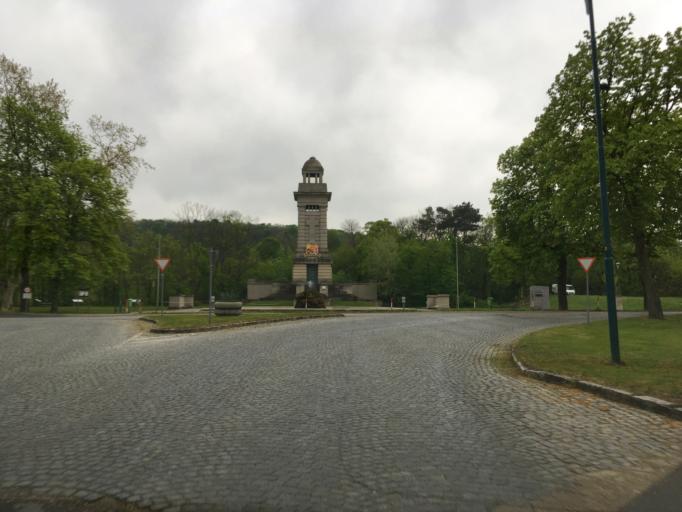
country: AT
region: Burgenland
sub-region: Politischer Bezirk Neusiedl am See
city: Bruckneudorf
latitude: 48.0169
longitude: 16.7791
